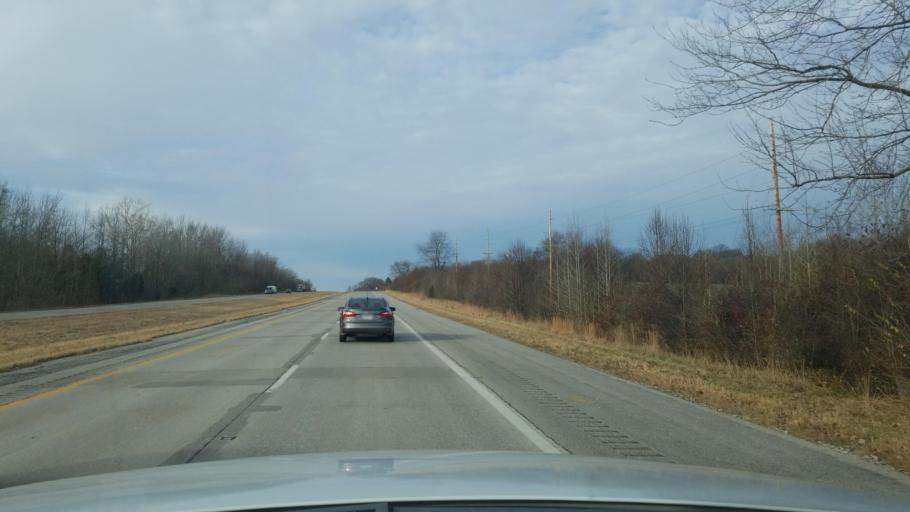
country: US
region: Kentucky
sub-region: Henderson County
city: Henderson
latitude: 37.9426
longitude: -87.7239
